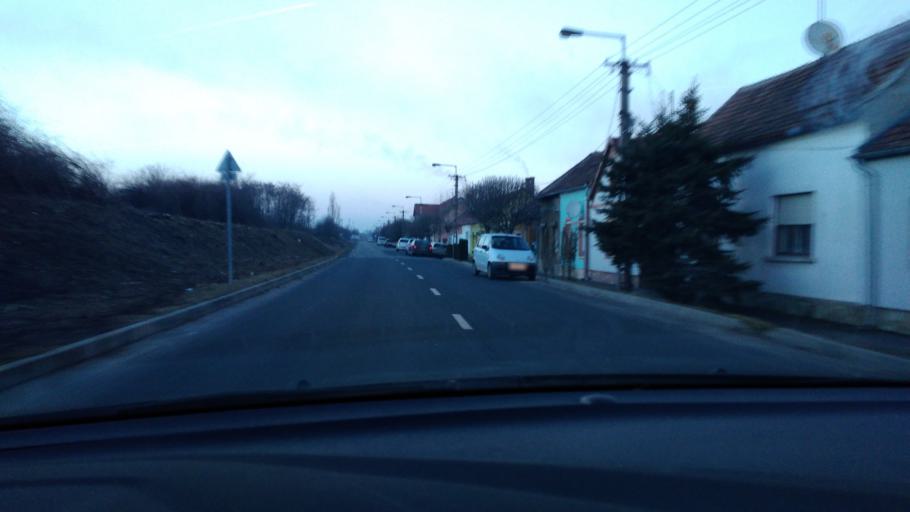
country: HU
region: Vas
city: Szombathely
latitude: 47.2241
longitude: 16.6399
